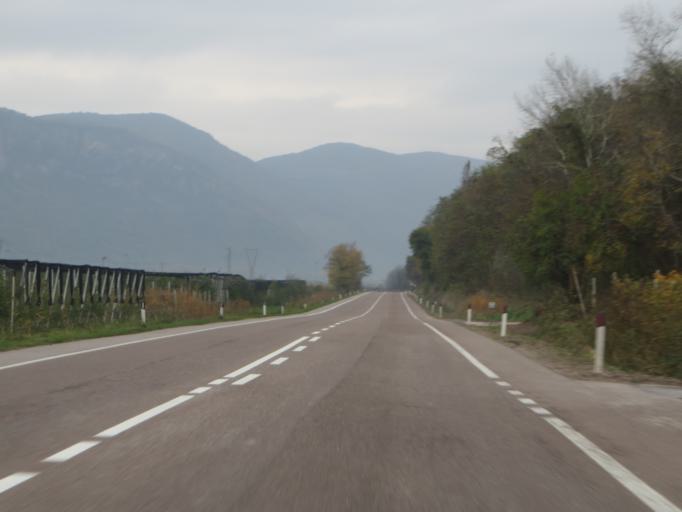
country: IT
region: Trentino-Alto Adige
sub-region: Bolzano
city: Bronzolo
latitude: 46.3798
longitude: 11.3177
